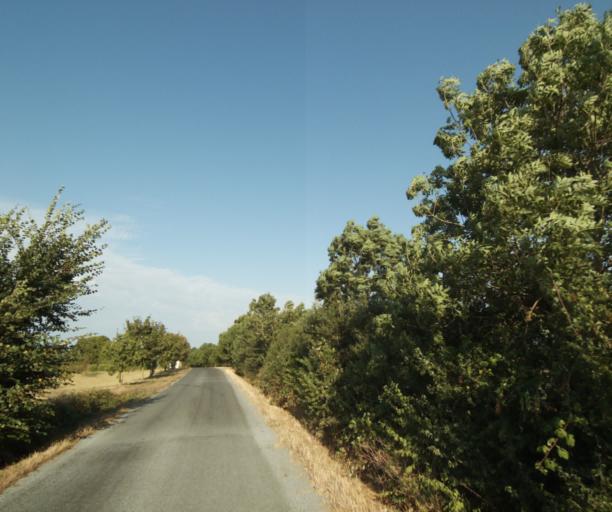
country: FR
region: Poitou-Charentes
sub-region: Departement de la Charente-Maritime
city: Muron
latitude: 45.9827
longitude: -0.8153
